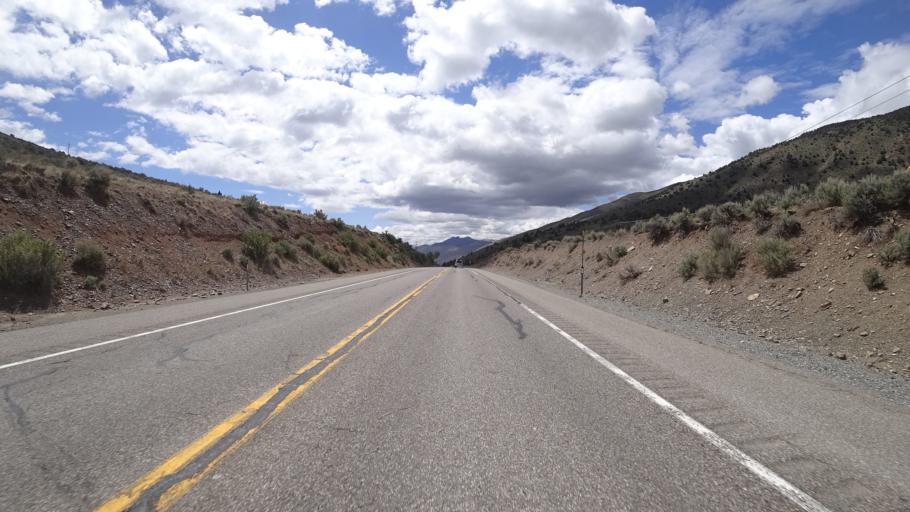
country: US
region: Nevada
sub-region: Lyon County
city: Smith Valley
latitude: 38.7123
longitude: -119.5535
